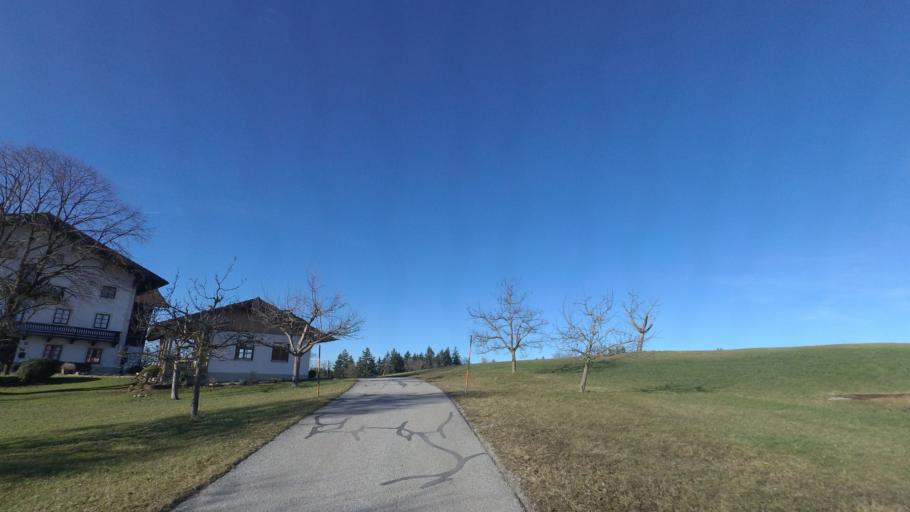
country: DE
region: Bavaria
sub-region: Upper Bavaria
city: Grabenstatt
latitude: 47.8369
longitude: 12.5702
